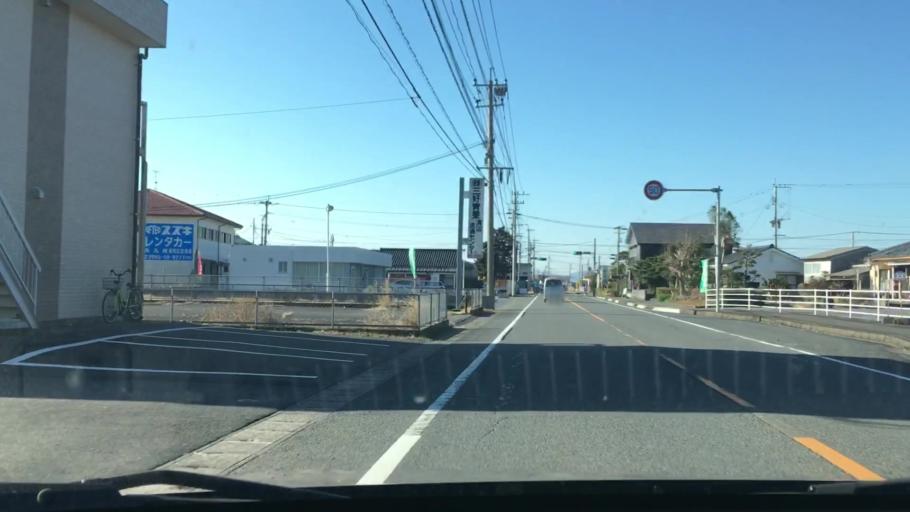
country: JP
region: Kagoshima
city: Kajiki
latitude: 31.7924
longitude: 130.7156
